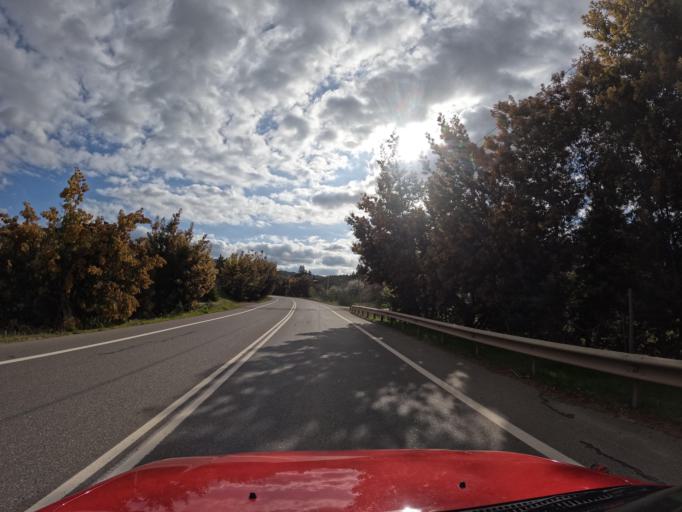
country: CL
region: Maule
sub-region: Provincia de Talca
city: Constitucion
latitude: -35.5553
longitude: -72.1317
